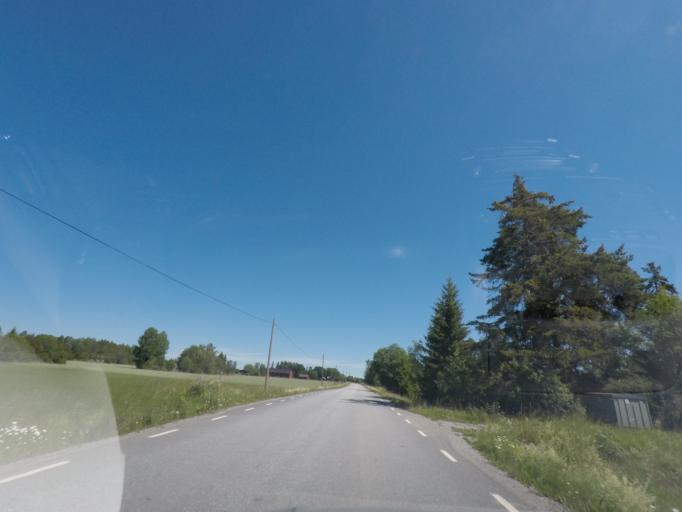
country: SE
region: Uppsala
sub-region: Enkopings Kommun
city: Irsta
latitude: 59.7051
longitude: 17.0080
